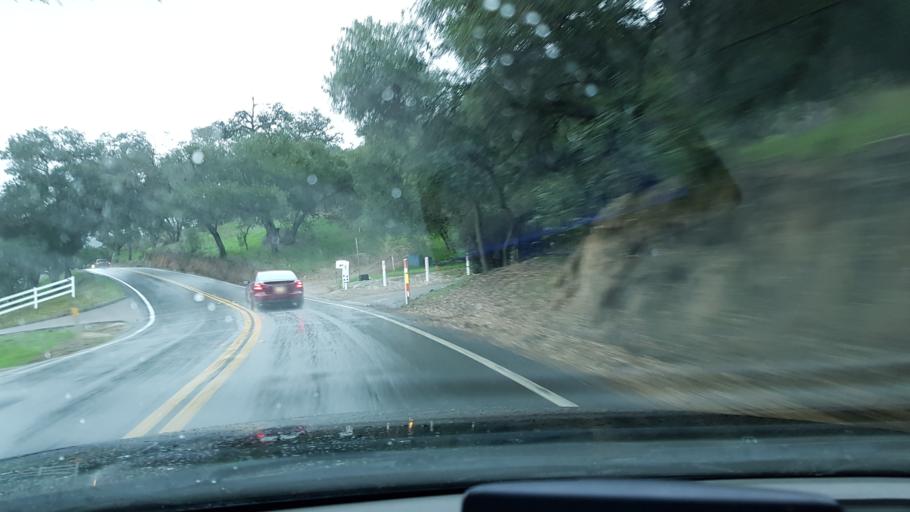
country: US
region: California
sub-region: San Diego County
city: Valley Center
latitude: 33.2055
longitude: -116.9798
